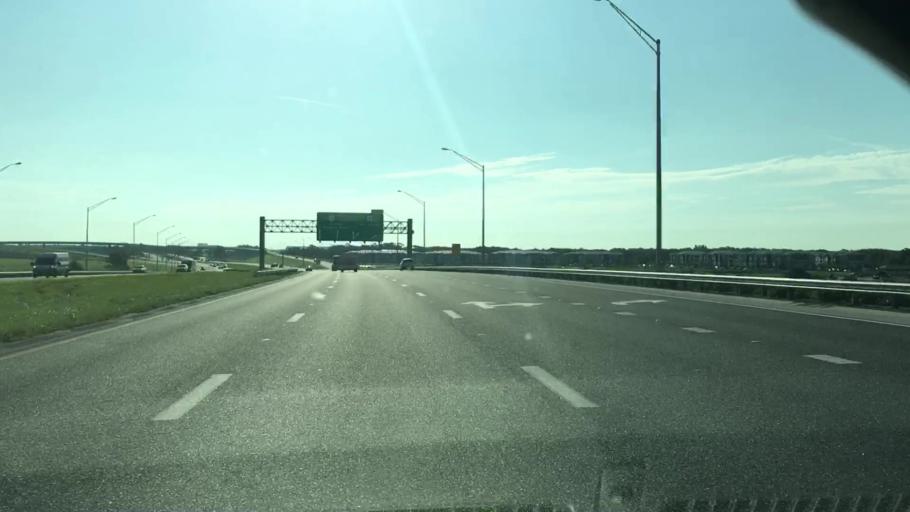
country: US
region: Florida
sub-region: Osceola County
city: Buenaventura Lakes
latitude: 28.3670
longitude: -81.3242
